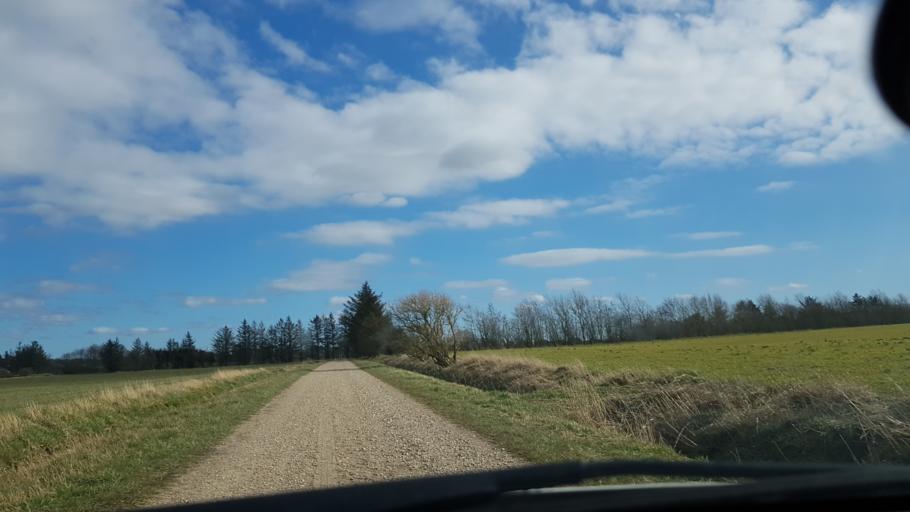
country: DK
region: South Denmark
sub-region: Esbjerg Kommune
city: Ribe
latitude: 55.2844
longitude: 8.8165
